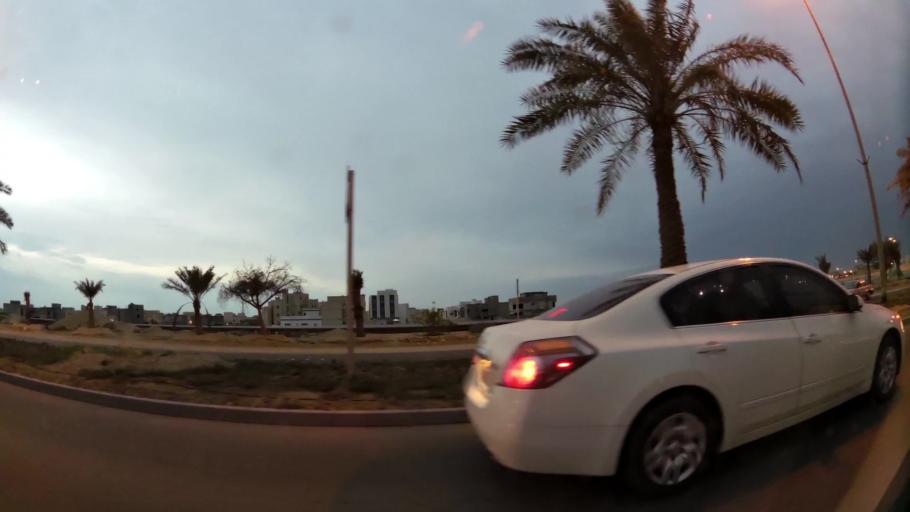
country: BH
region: Central Governorate
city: Madinat Hamad
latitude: 26.1413
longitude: 50.5051
